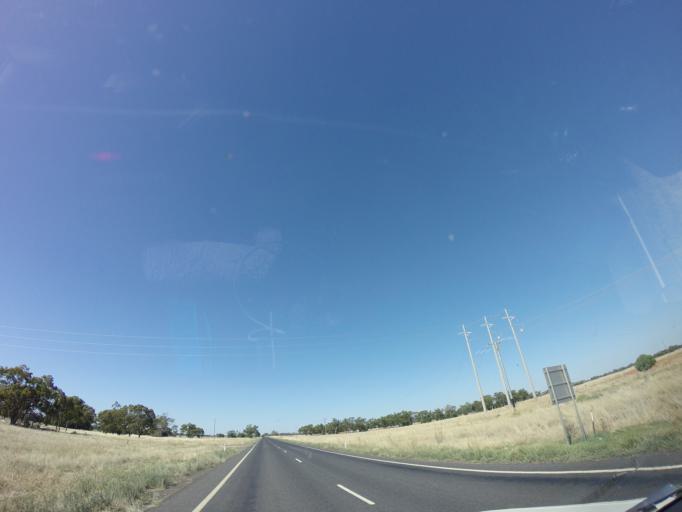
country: AU
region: New South Wales
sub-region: Bogan
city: Nyngan
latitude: -31.8325
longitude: 147.7237
